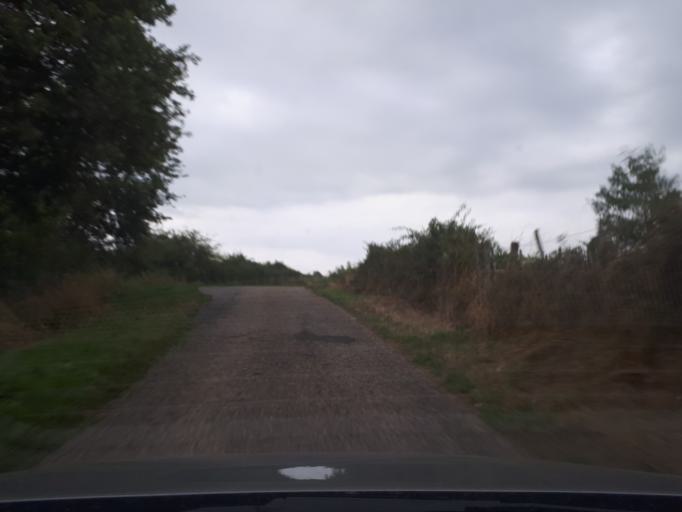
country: FR
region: Rhone-Alpes
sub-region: Departement de la Loire
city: Civens
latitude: 45.7540
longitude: 4.2744
